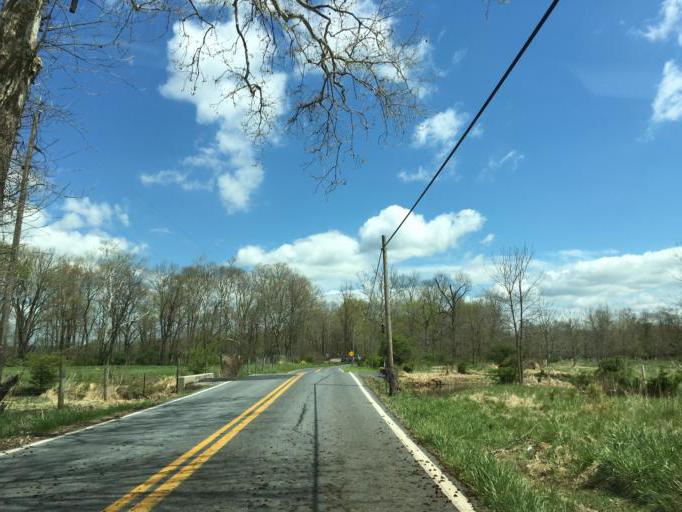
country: US
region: Maryland
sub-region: Frederick County
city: Thurmont
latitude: 39.6310
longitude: -77.3732
